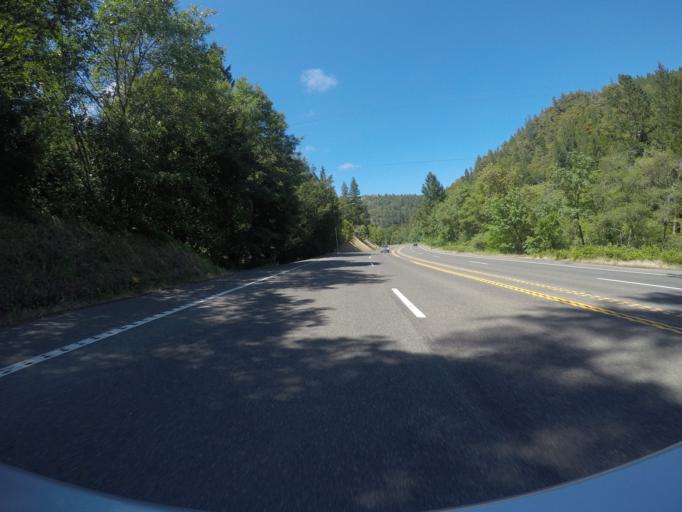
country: US
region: California
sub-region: Mendocino County
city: Brooktrails
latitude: 39.5477
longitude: -123.4249
